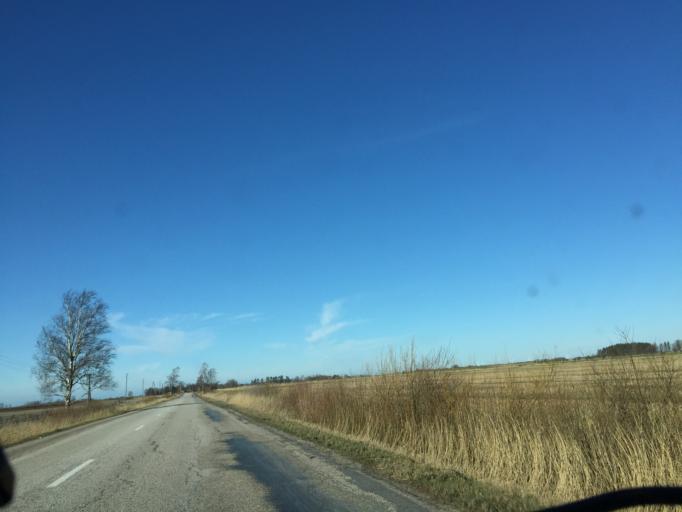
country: LV
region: Ventspils Rajons
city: Piltene
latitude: 57.3047
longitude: 21.6435
